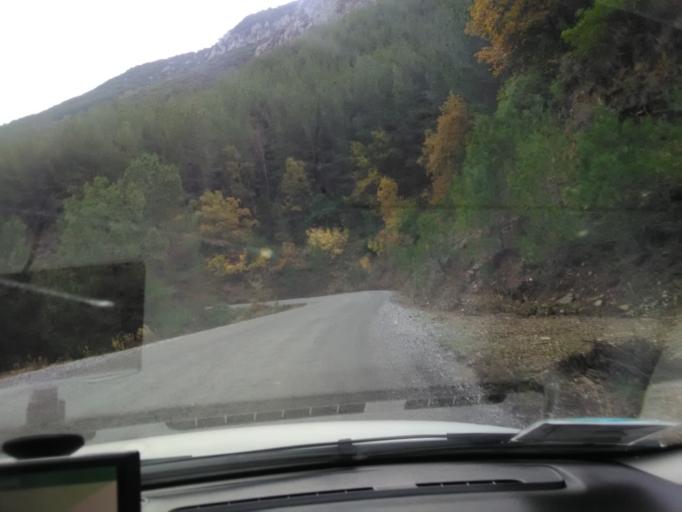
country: TR
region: Antalya
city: Gazipasa
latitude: 36.2464
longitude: 32.4305
